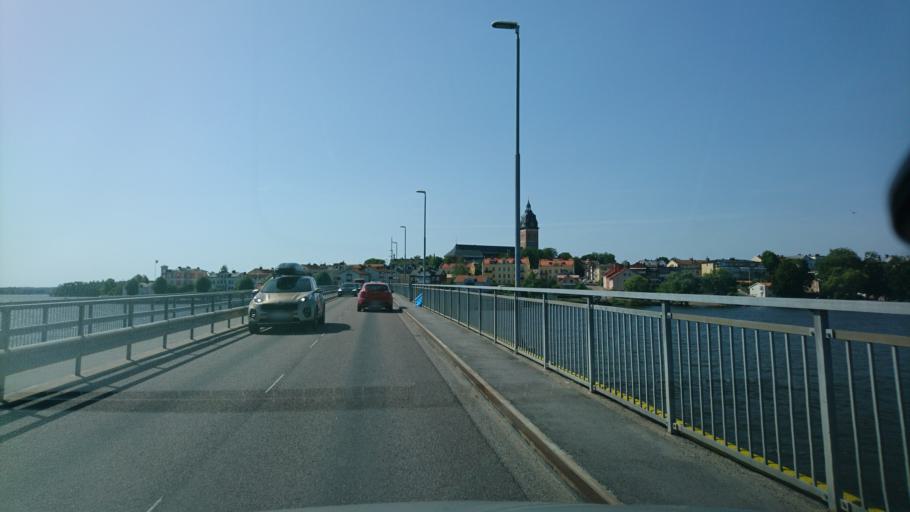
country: SE
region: Soedermanland
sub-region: Strangnas Kommun
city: Strangnas
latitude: 59.3797
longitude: 17.0388
